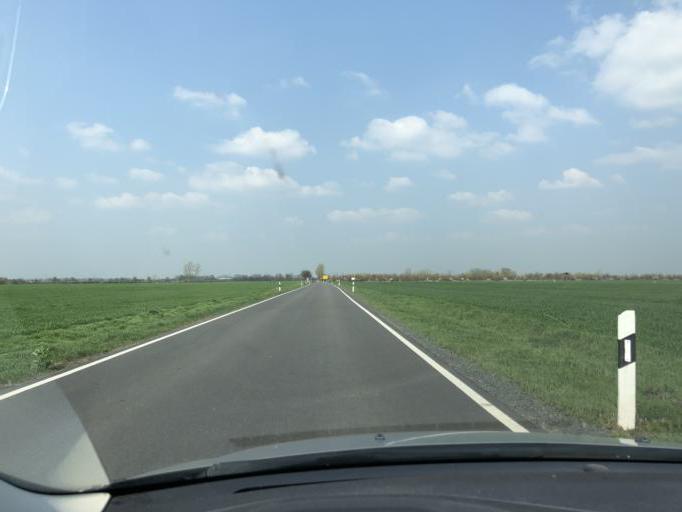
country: DE
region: Saxony
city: Wiedemar
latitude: 51.4918
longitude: 12.2135
